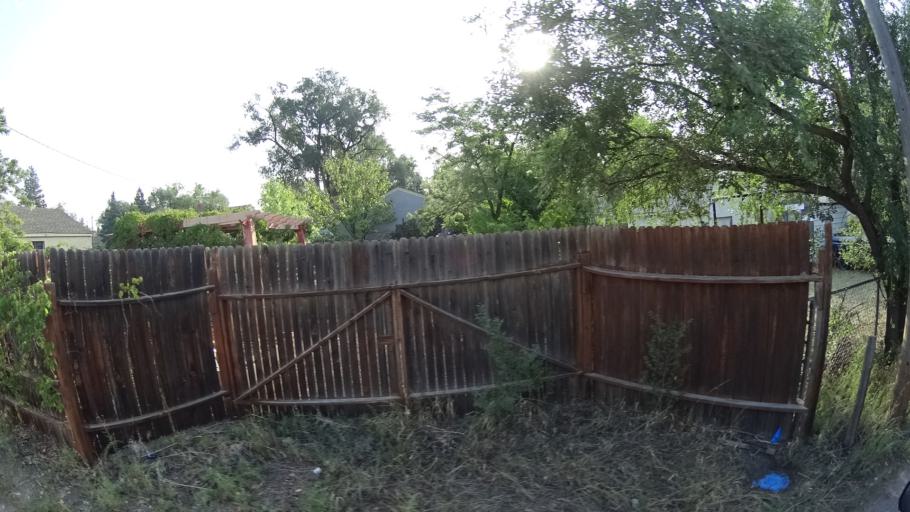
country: US
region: Colorado
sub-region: El Paso County
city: Colorado Springs
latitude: 38.8460
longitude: -104.7880
